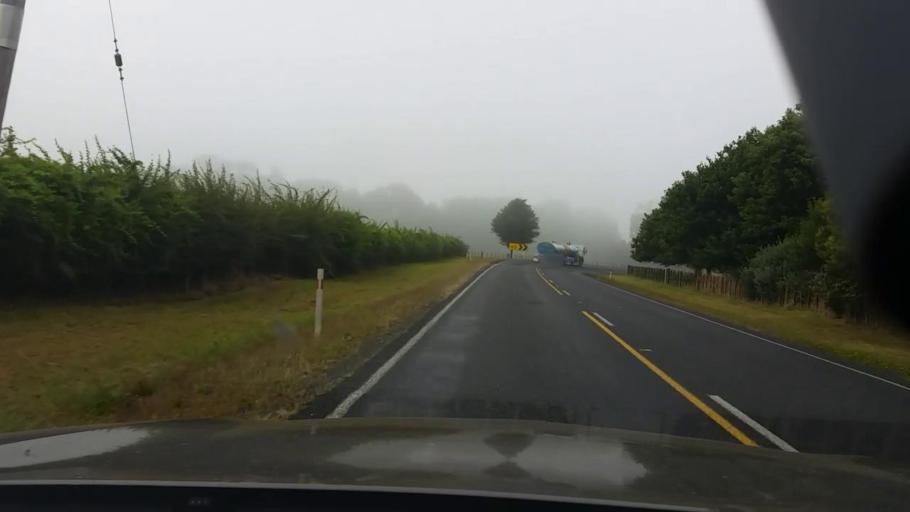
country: NZ
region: Waikato
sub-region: Hamilton City
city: Hamilton
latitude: -37.6503
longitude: 175.2980
